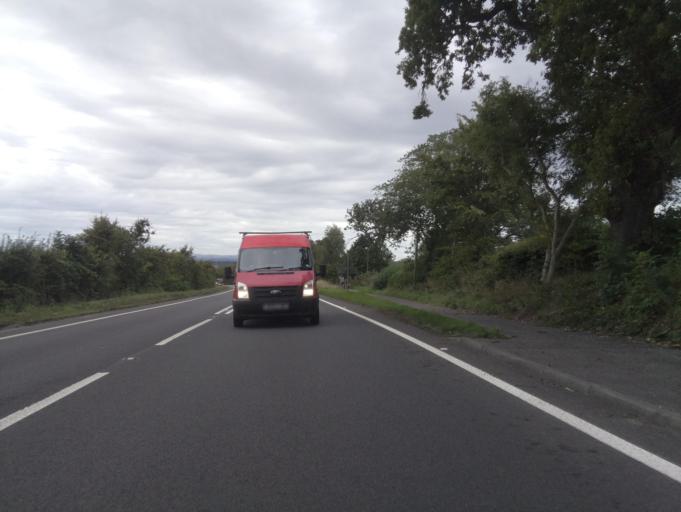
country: GB
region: Scotland
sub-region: Fife
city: Kincardine
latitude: 56.0648
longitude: -3.6922
